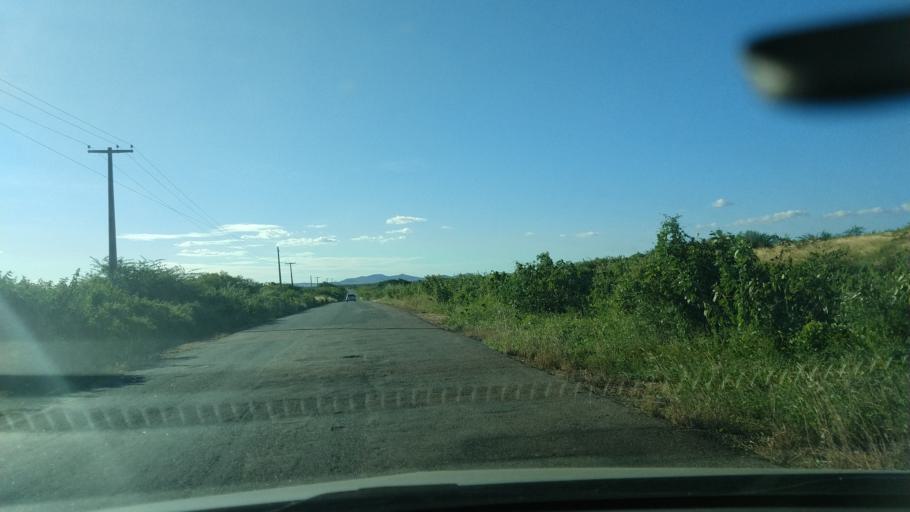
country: BR
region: Rio Grande do Norte
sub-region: Sao Jose Do Campestre
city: Sao Jose do Campestre
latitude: -6.4001
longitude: -35.6557
